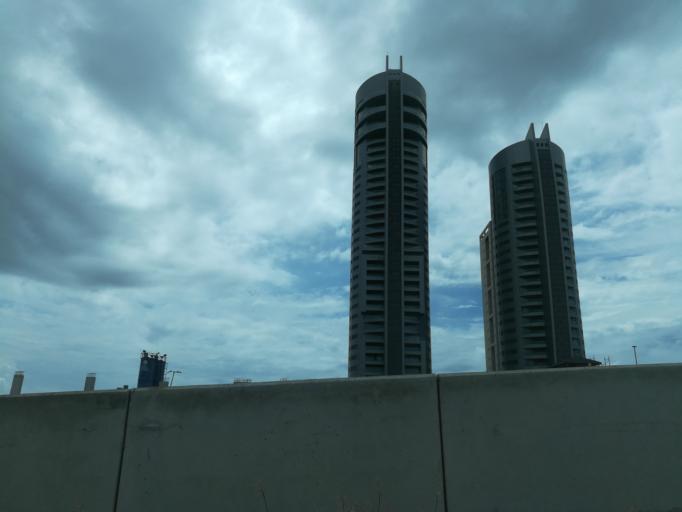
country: NG
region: Lagos
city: Lagos
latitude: 6.4098
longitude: 3.4090
